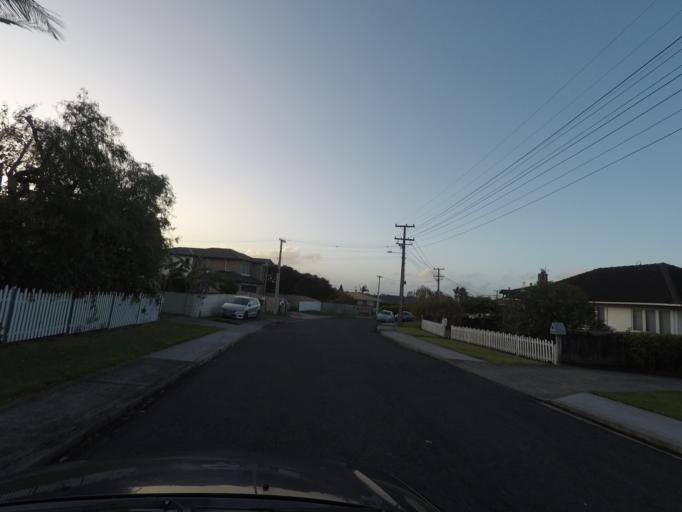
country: NZ
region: Auckland
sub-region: Auckland
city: Rosebank
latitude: -36.8362
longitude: 174.6444
